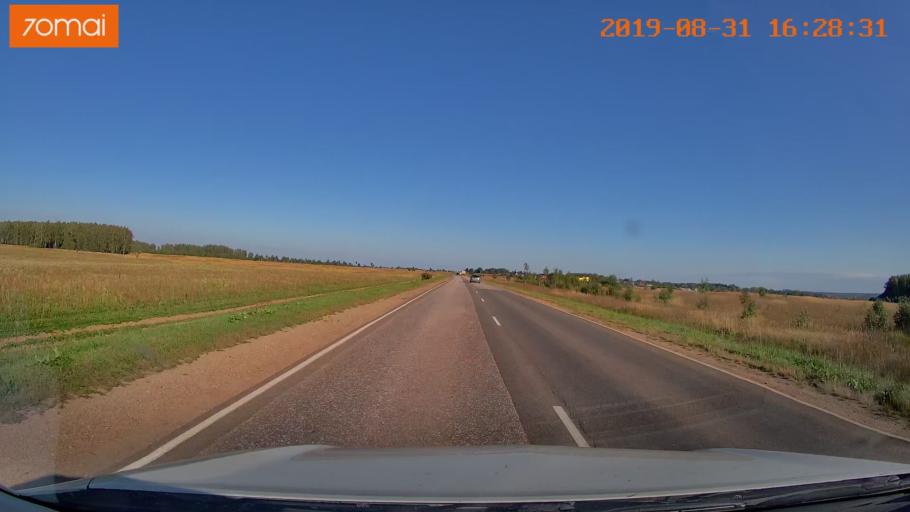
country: RU
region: Kaluga
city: Babynino
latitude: 54.5095
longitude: 35.7822
